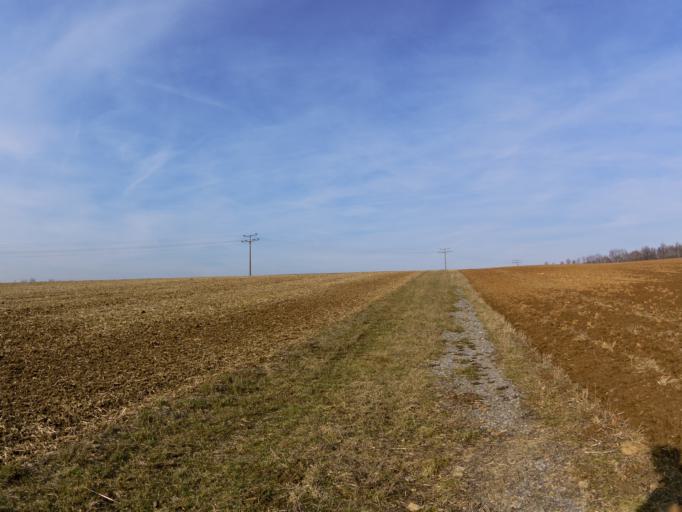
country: DE
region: Bavaria
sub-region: Regierungsbezirk Unterfranken
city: Kurnach
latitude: 49.8296
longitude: 10.0354
